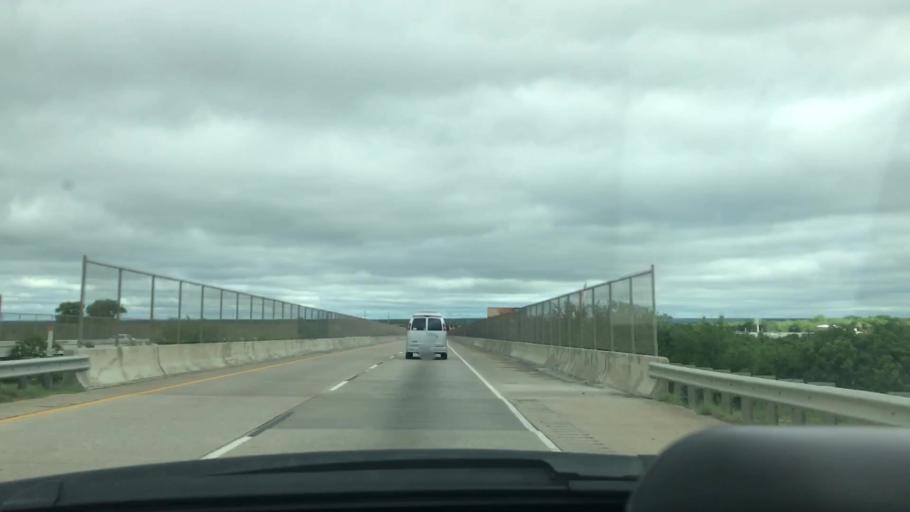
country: US
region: Texas
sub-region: Grayson County
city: Denison
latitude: 33.7697
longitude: -96.5849
